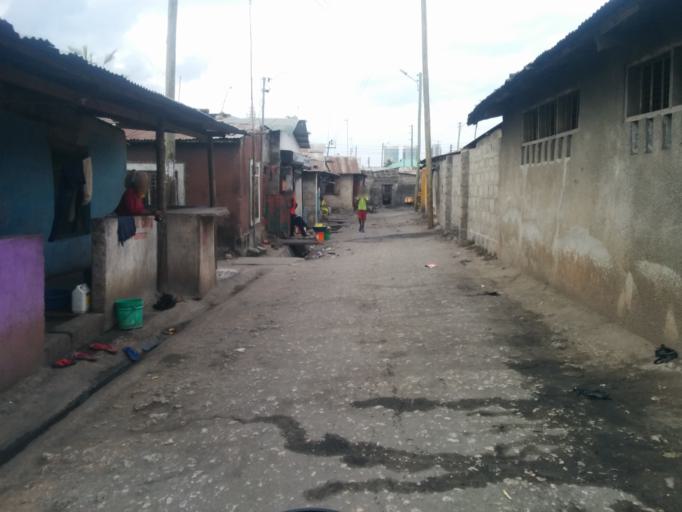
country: TZ
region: Dar es Salaam
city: Dar es Salaam
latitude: -6.8356
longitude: 39.2770
